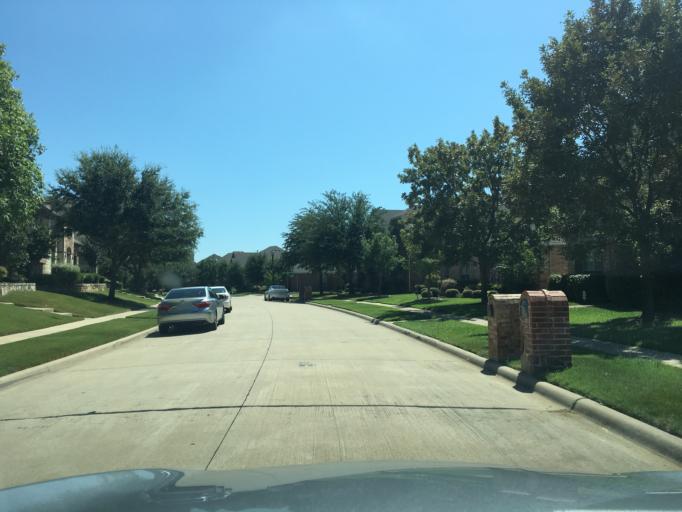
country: US
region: Texas
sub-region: Dallas County
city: Sachse
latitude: 32.9665
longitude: -96.6159
